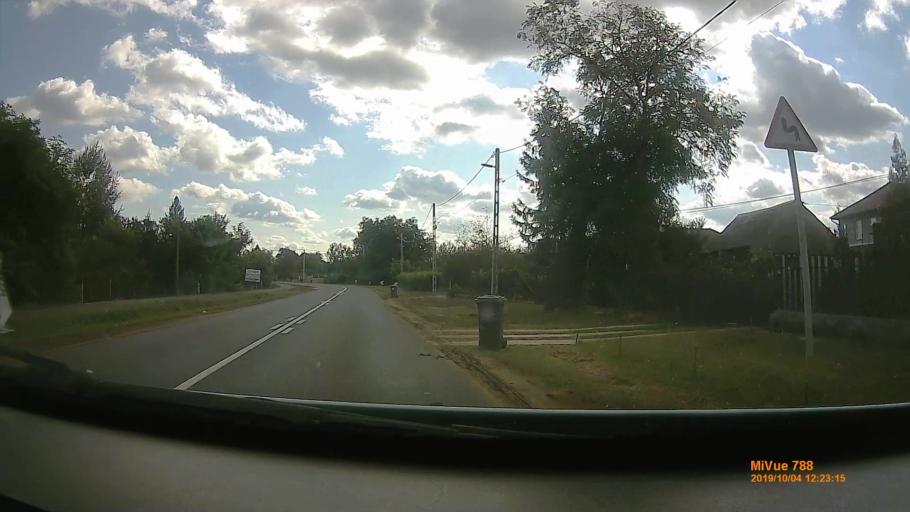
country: HU
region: Szabolcs-Szatmar-Bereg
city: Kotaj
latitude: 48.0068
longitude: 21.6960
